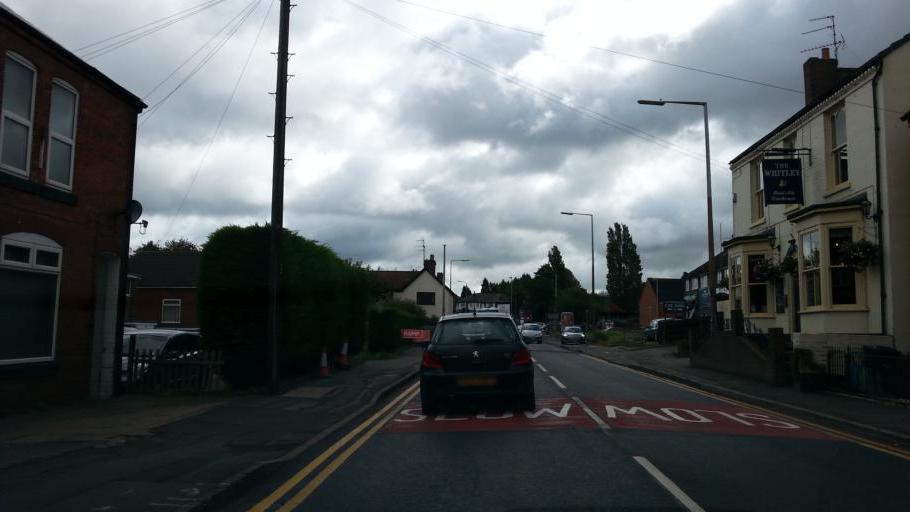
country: GB
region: England
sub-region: Dudley
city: Halesowen
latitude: 52.4539
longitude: -2.0647
